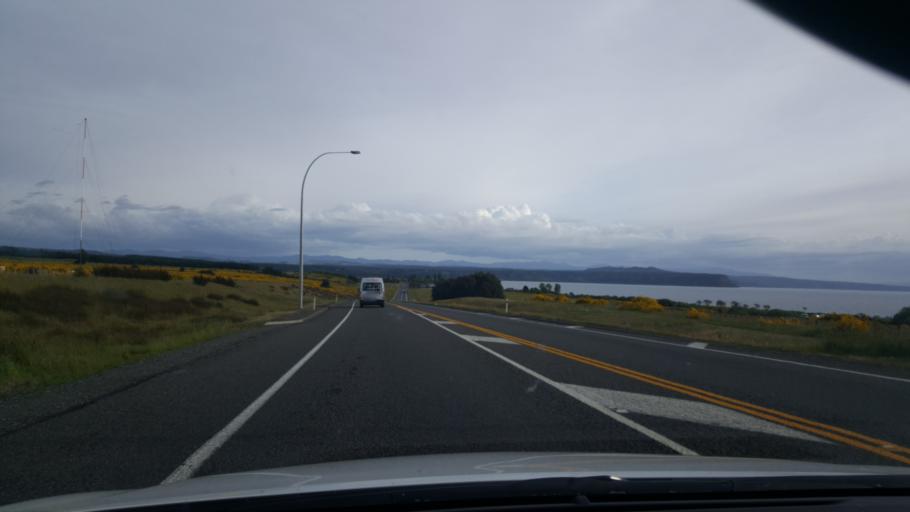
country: NZ
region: Waikato
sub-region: Taupo District
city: Taupo
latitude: -38.7415
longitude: 176.0728
